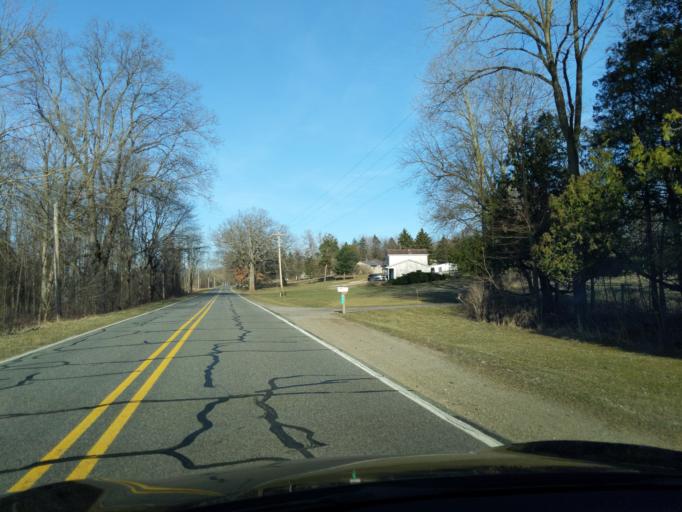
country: US
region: Michigan
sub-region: Ionia County
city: Saranac
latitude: 42.9369
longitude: -85.1884
